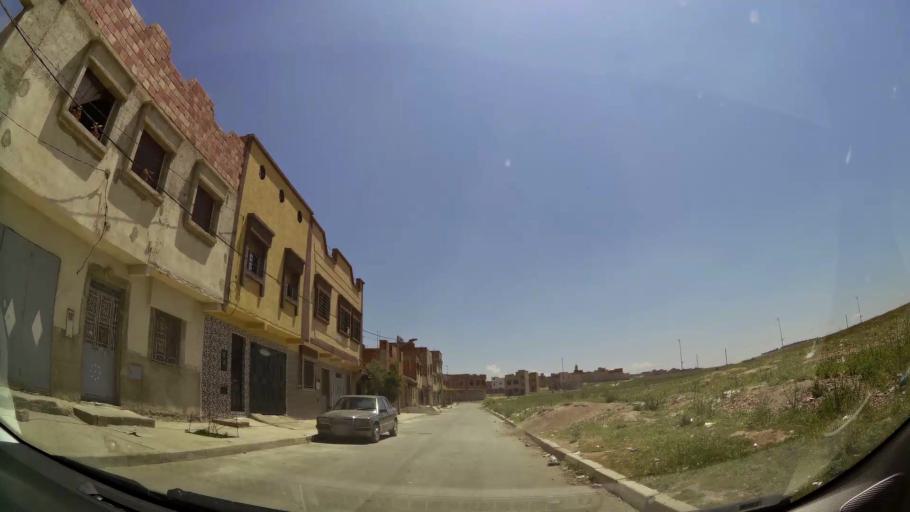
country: MA
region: Oriental
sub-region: Oujda-Angad
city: Oujda
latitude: 34.6904
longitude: -1.9537
